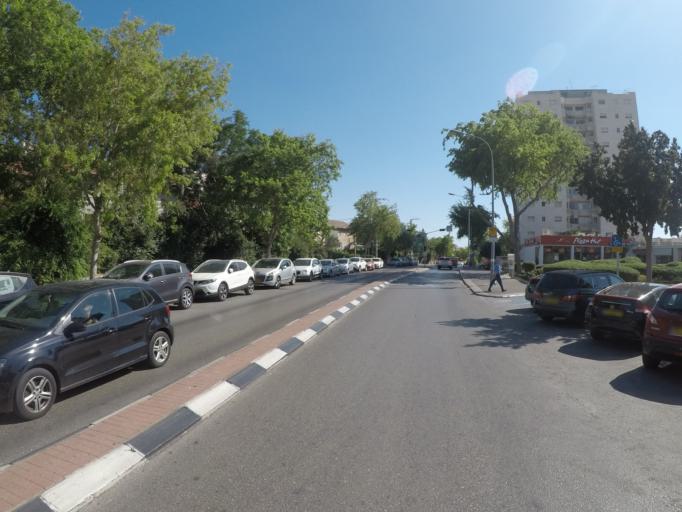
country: IL
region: Tel Aviv
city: Ramat Gan
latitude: 32.1069
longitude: 34.7978
